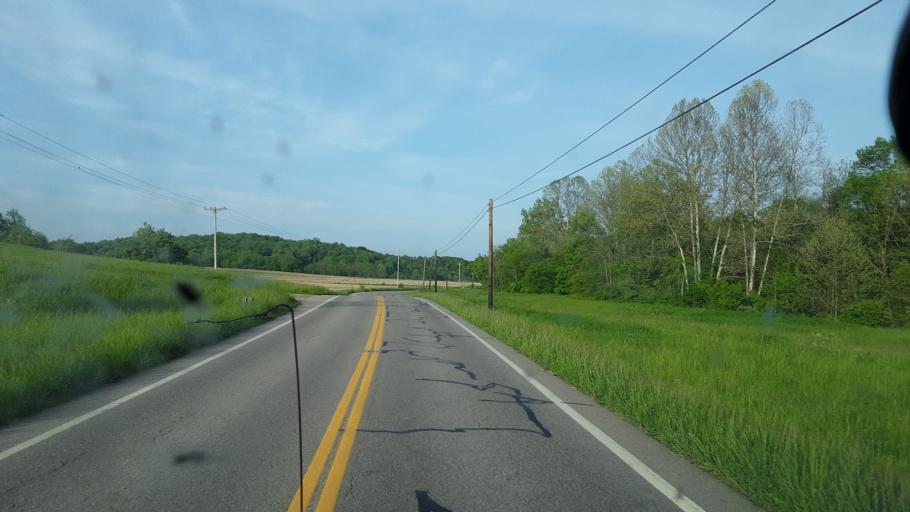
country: US
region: Ohio
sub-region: Ross County
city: Kingston
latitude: 39.4955
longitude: -82.7155
